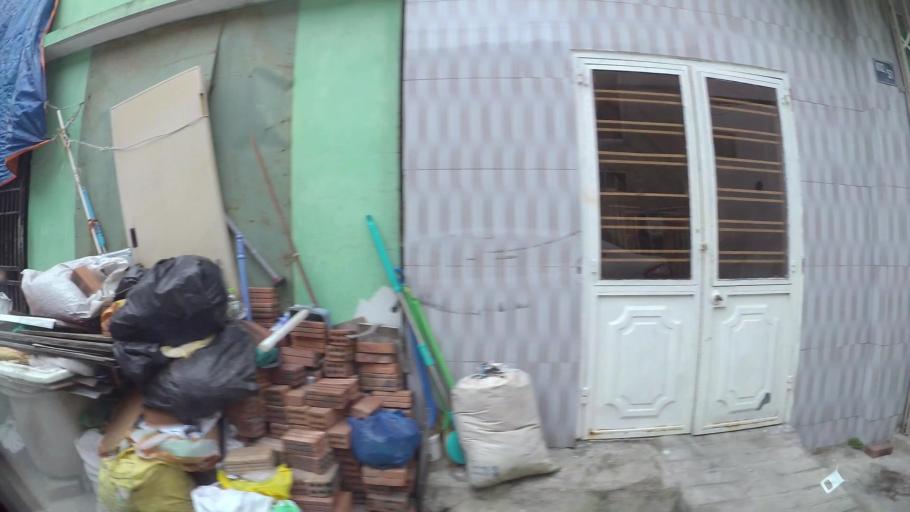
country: VN
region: Da Nang
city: Thanh Khe
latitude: 16.0721
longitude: 108.1991
